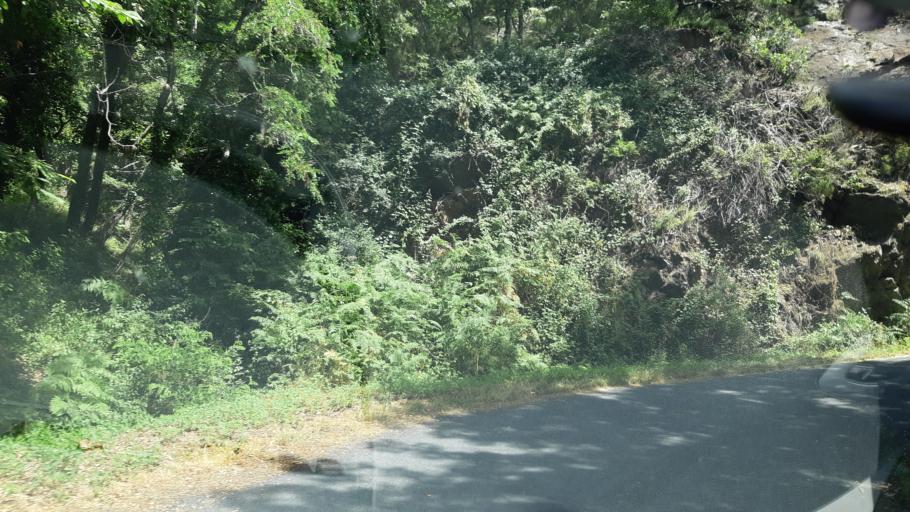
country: FR
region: Languedoc-Roussillon
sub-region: Departement des Pyrenees-Orientales
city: Arles
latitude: 42.5317
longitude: 2.6103
